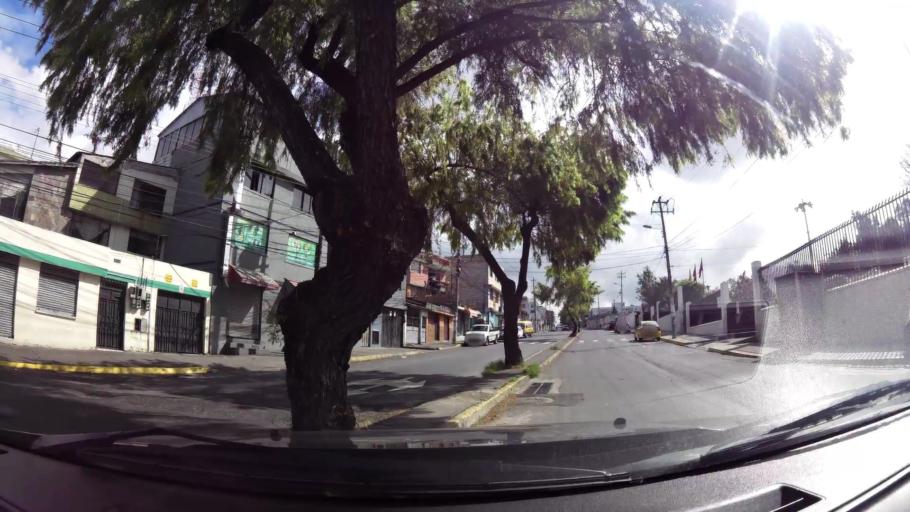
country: EC
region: Pichincha
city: Quito
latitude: -0.1624
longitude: -78.4740
